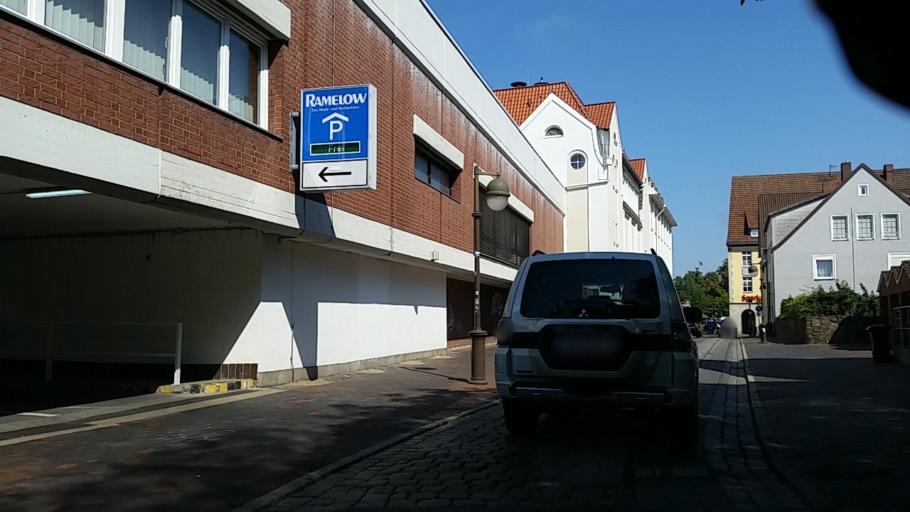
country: DE
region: Lower Saxony
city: Uelzen
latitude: 52.9644
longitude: 10.5579
